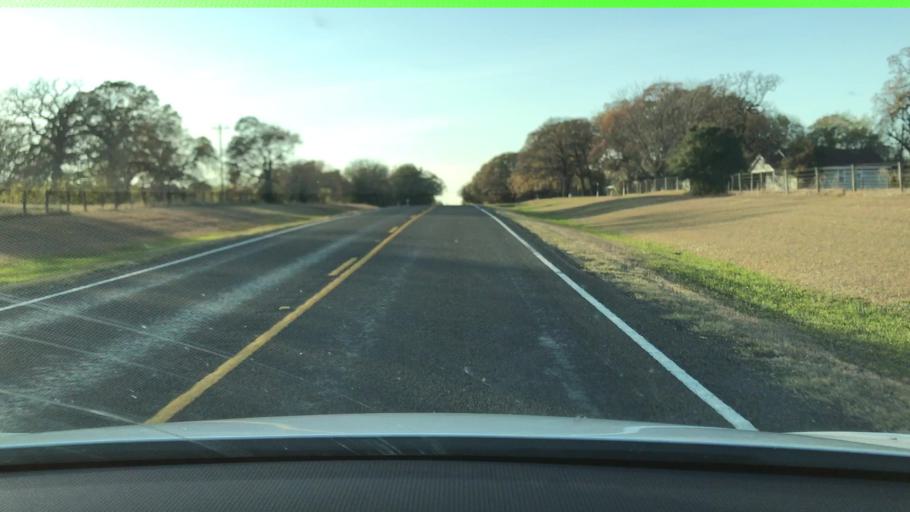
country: US
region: Texas
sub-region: Kaufman County
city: Kemp
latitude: 32.5712
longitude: -96.1488
